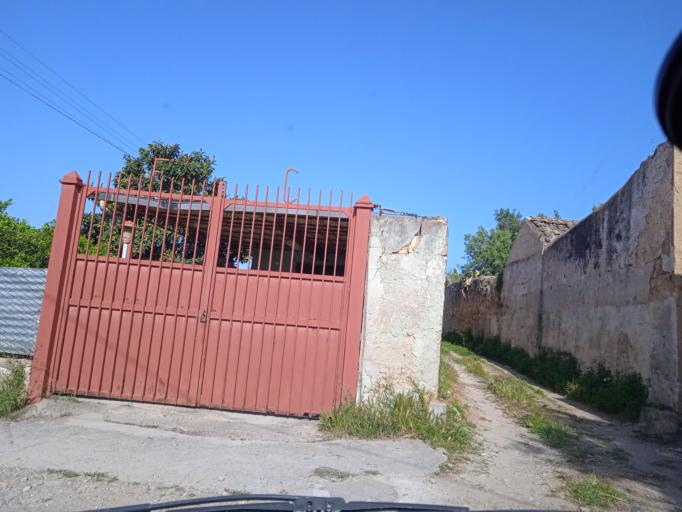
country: IT
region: Sicily
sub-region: Palermo
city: Villabate
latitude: 38.0800
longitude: 13.4514
